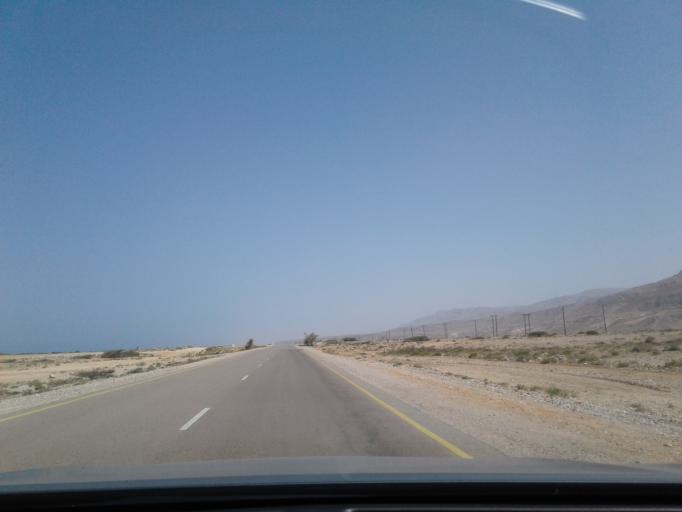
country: OM
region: Ash Sharqiyah
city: Al Qabil
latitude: 23.0405
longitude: 59.0740
